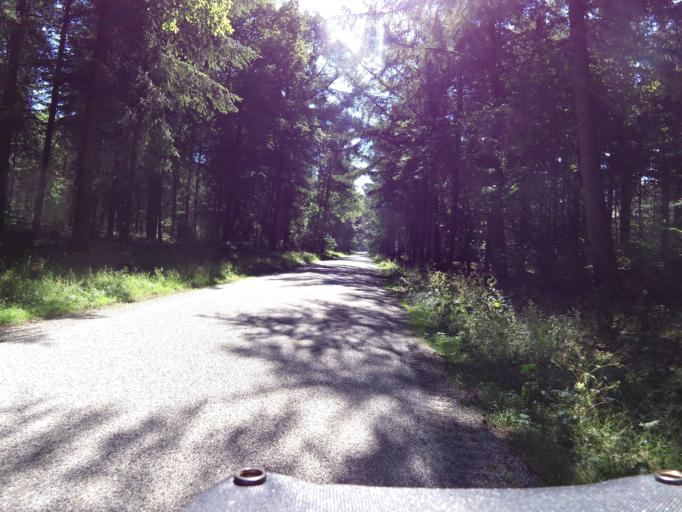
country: NL
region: Overijssel
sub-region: Gemeente Twenterand
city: Den Ham
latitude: 52.5345
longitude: 6.4972
